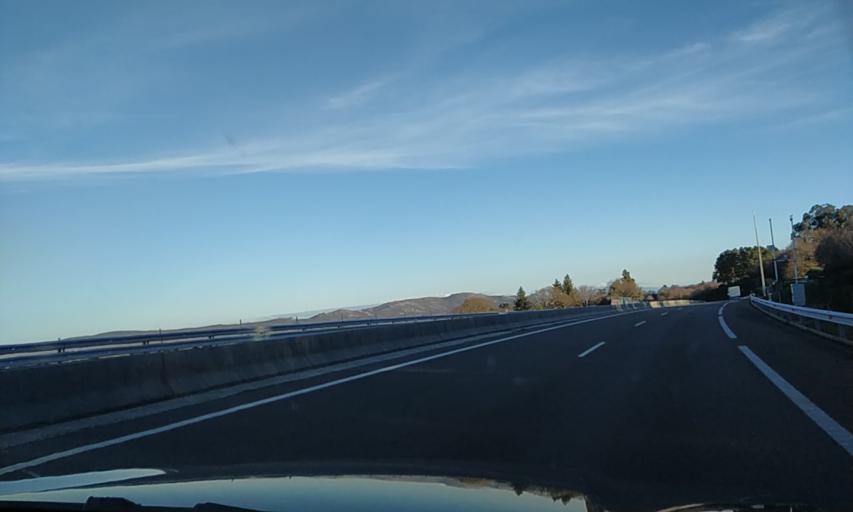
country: ES
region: Galicia
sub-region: Provincia de Pontevedra
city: Dozon
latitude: 42.5603
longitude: -8.0303
